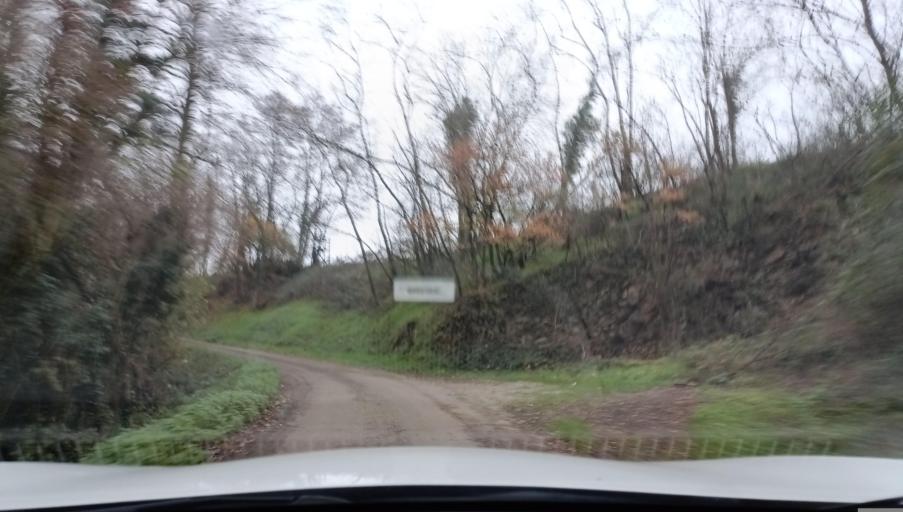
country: FR
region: Rhone-Alpes
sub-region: Departement de l'Isere
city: Chuzelles
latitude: 45.5686
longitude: 4.8715
